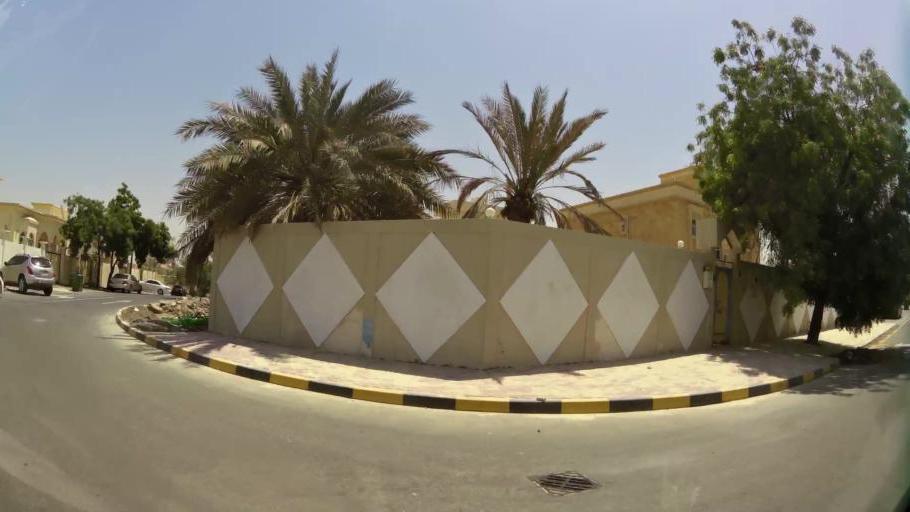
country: AE
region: Ajman
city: Ajman
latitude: 25.4037
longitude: 55.5145
